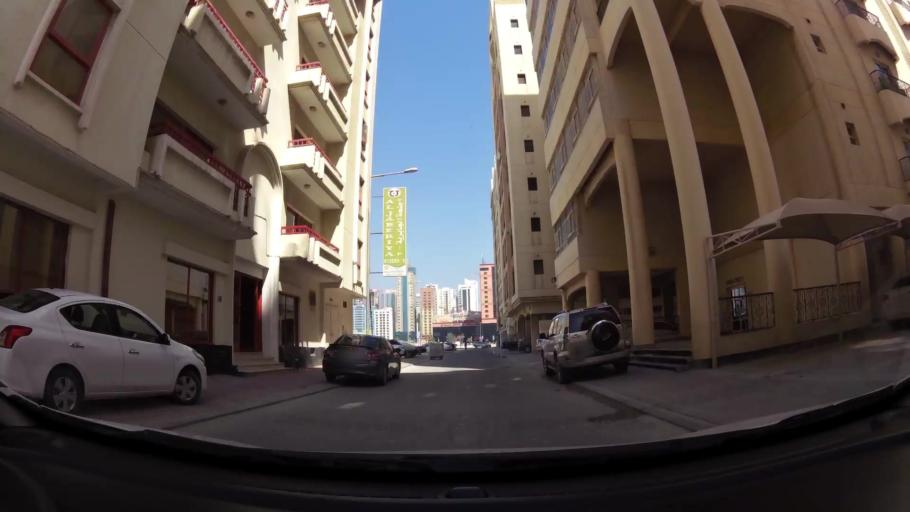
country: BH
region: Manama
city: Manama
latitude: 26.2140
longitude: 50.6077
